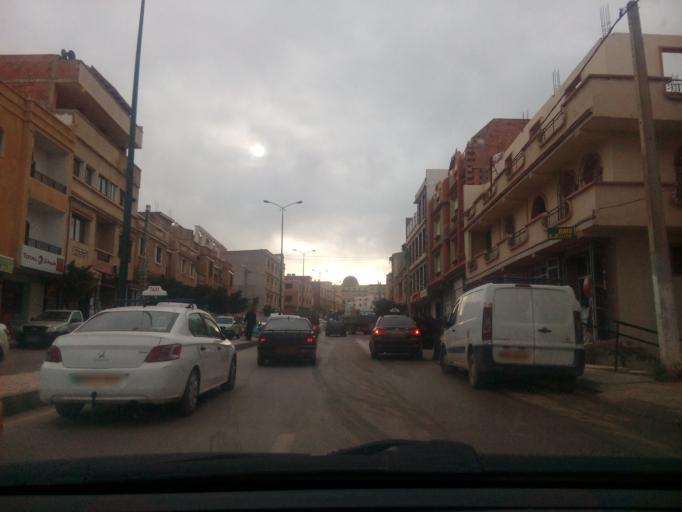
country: DZ
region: Tlemcen
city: Mansoura
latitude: 34.8821
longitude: -1.3502
